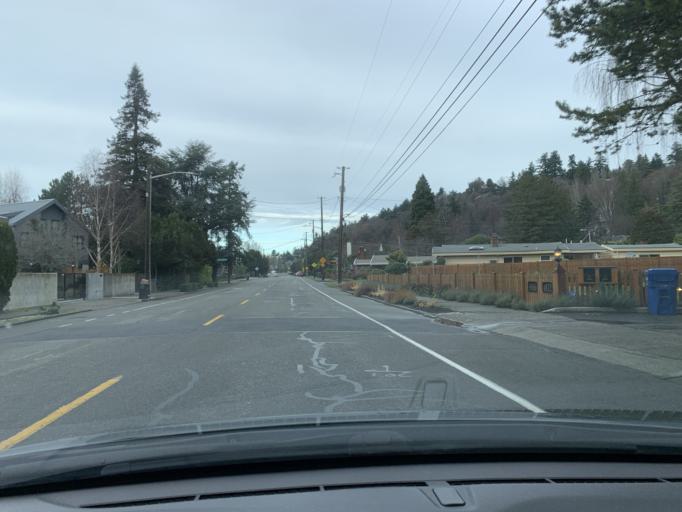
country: US
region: Washington
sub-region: King County
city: White Center
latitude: 47.5578
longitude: -122.4013
